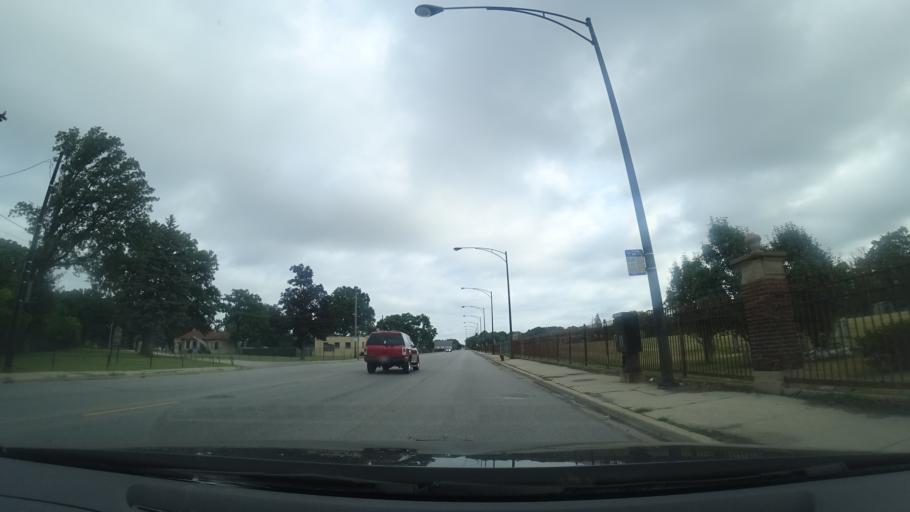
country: US
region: Illinois
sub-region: Cook County
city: Lincolnwood
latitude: 41.9790
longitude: -87.7283
